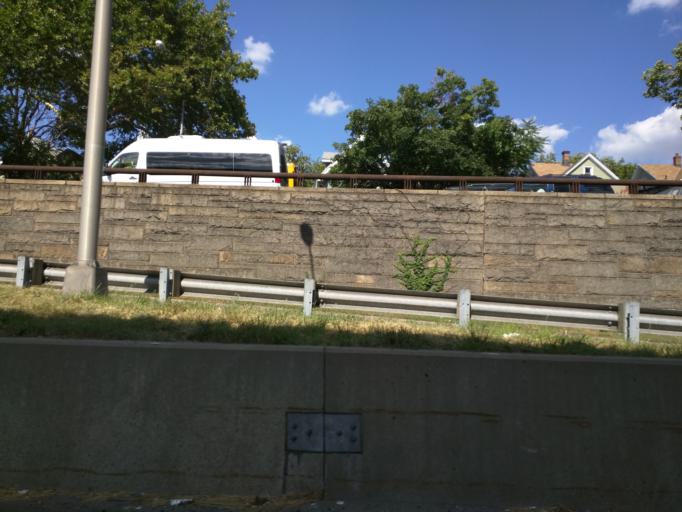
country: US
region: New York
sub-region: Queens County
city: Jamaica
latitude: 40.6958
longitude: -73.8126
